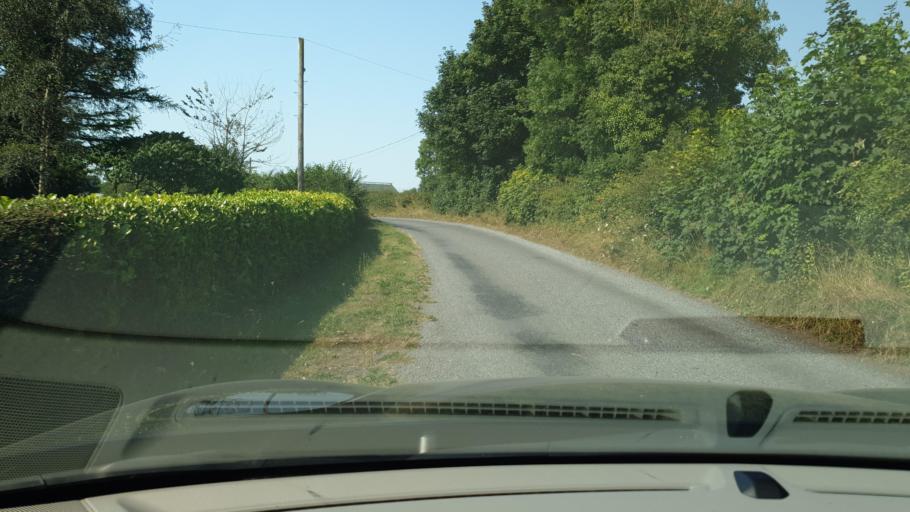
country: IE
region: Leinster
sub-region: An Mhi
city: Athboy
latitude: 53.6074
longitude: -6.9883
